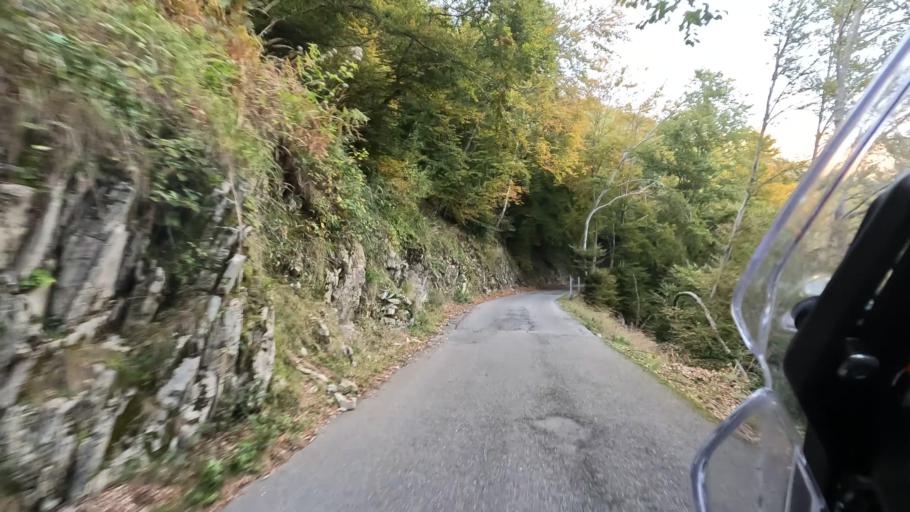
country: IT
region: Lombardy
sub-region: Provincia di Como
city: Pigra
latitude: 45.9686
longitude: 9.1197
